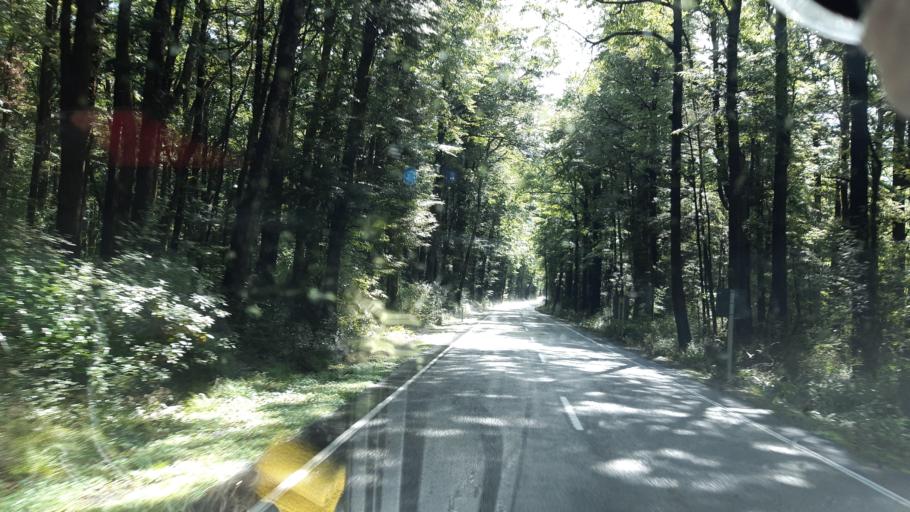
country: NZ
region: Canterbury
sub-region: Hurunui District
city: Amberley
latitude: -42.3773
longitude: 172.2754
